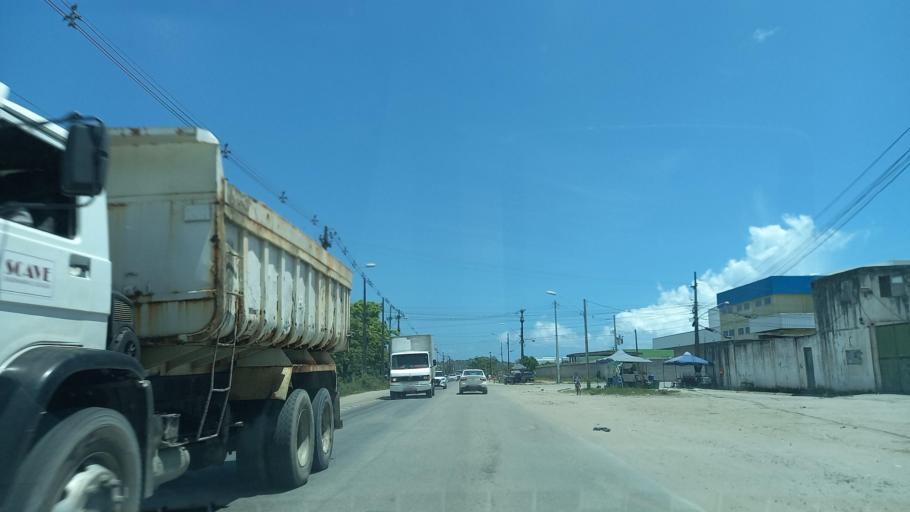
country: BR
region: Pernambuco
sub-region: Jaboatao Dos Guararapes
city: Jaboatao
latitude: -8.1566
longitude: -34.9674
